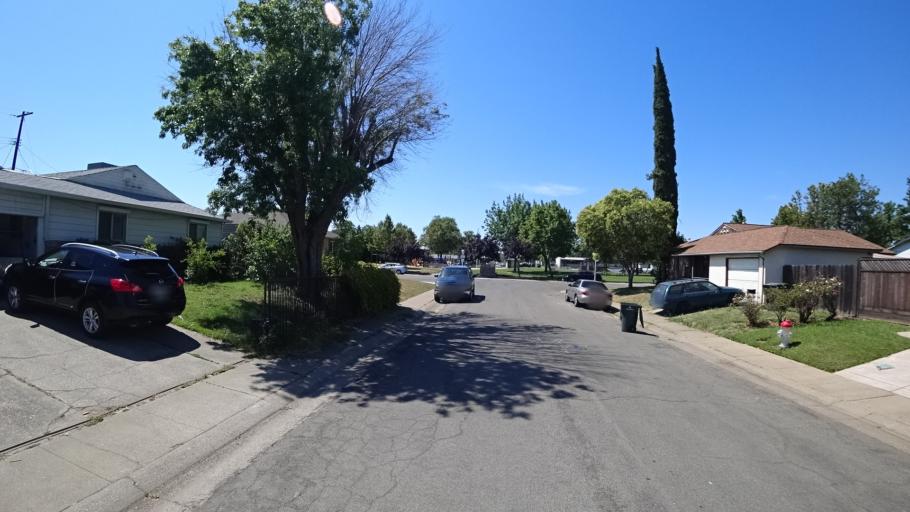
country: US
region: California
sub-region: Sacramento County
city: Florin
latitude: 38.5283
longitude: -121.4169
